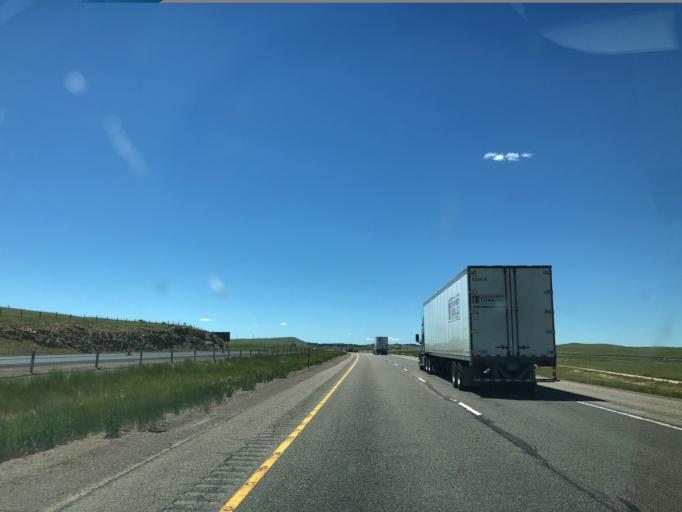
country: US
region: Wyoming
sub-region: Laramie County
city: Cheyenne
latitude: 41.0964
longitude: -105.1901
